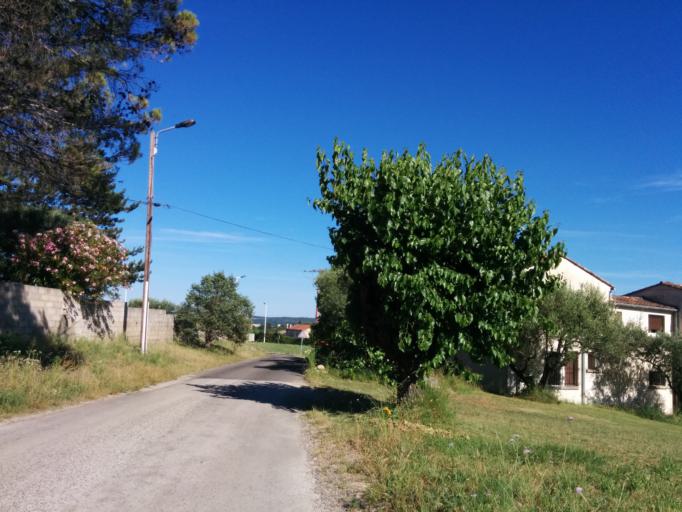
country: FR
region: Languedoc-Roussillon
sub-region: Departement du Gard
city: Saint-Christol-les-Ales
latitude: 44.0921
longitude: 4.0635
